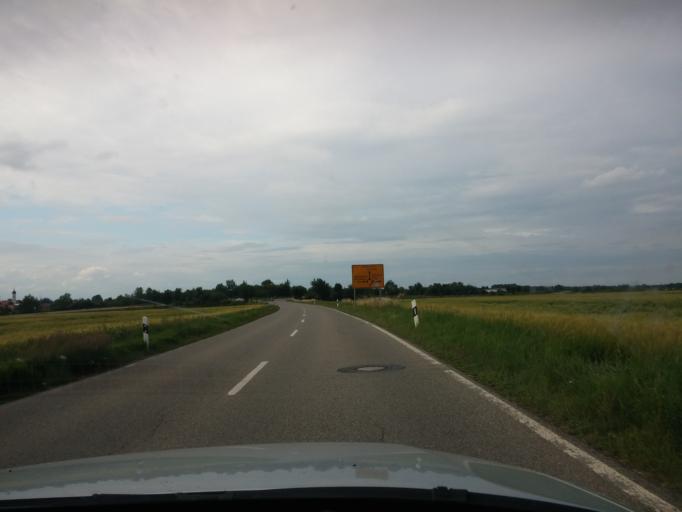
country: DE
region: Bavaria
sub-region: Upper Bavaria
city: Zorneding
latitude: 48.0720
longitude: 11.8233
